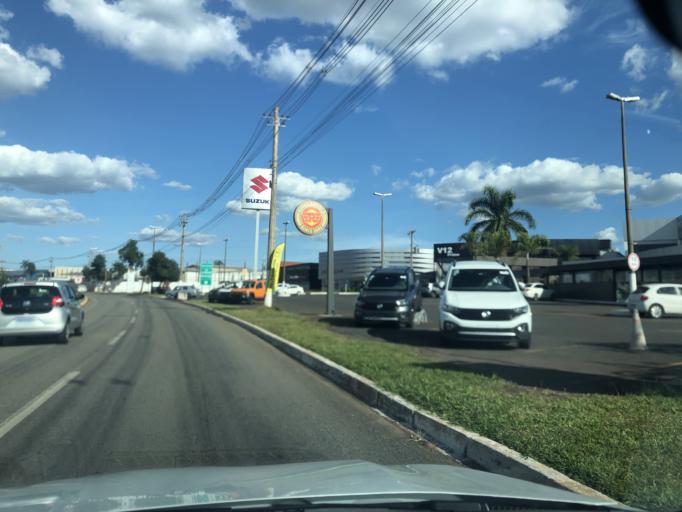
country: BR
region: Federal District
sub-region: Brasilia
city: Brasilia
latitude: -15.8701
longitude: -47.9357
